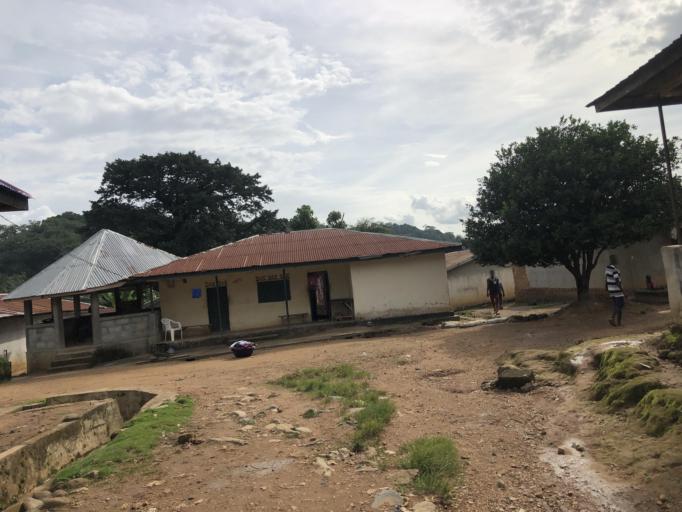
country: SL
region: Northern Province
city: Bumbuna
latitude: 9.0421
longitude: -11.7413
